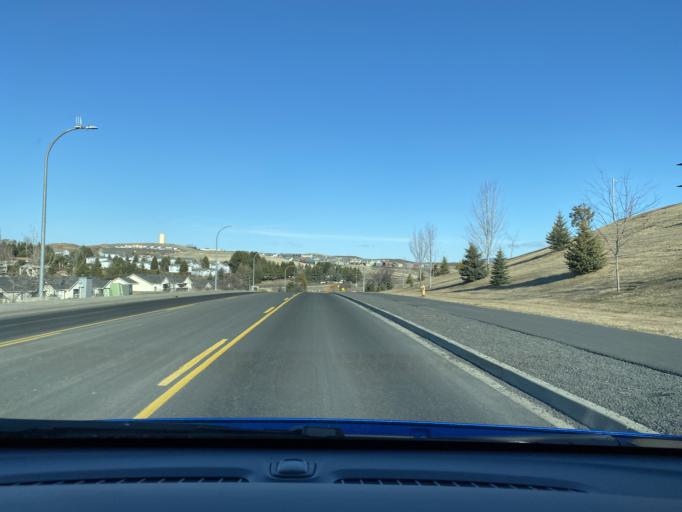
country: US
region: Washington
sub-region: Whitman County
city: Pullman
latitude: 46.7473
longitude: -117.1689
